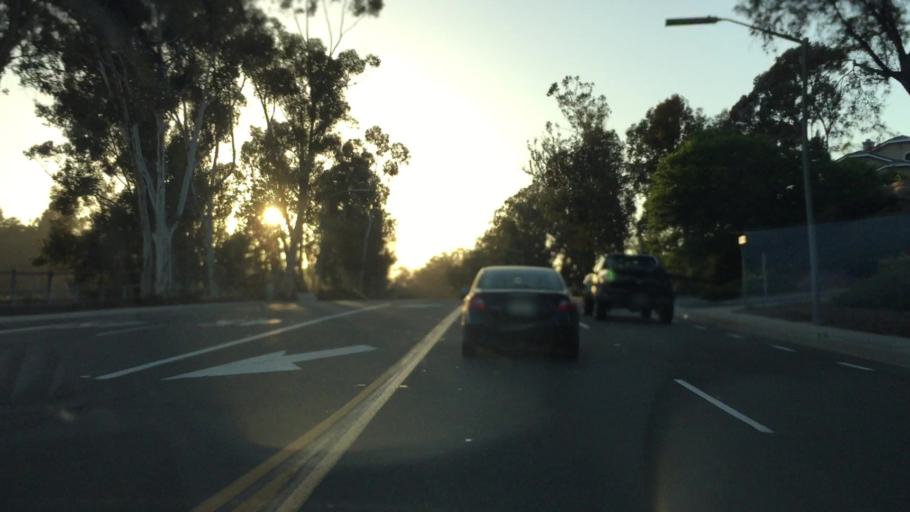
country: US
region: California
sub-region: San Diego County
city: Poway
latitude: 32.9752
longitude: -117.0441
